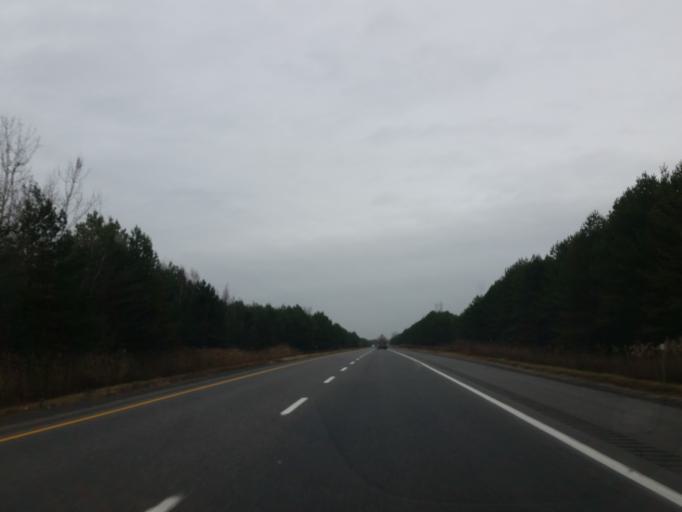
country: CA
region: Quebec
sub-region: Mauricie
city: Becancour
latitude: 46.5276
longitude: -72.2828
